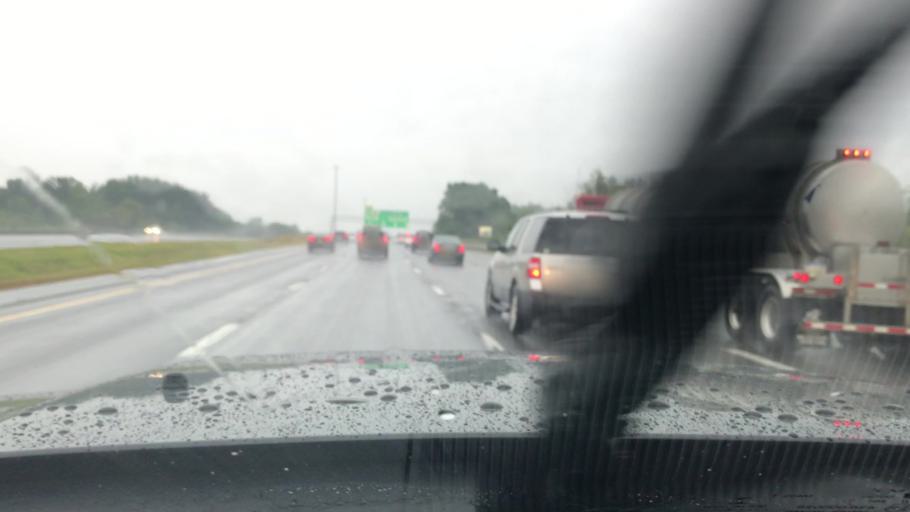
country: US
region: New Hampshire
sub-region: Rockingham County
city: Greenland
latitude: 43.0488
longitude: -70.8125
